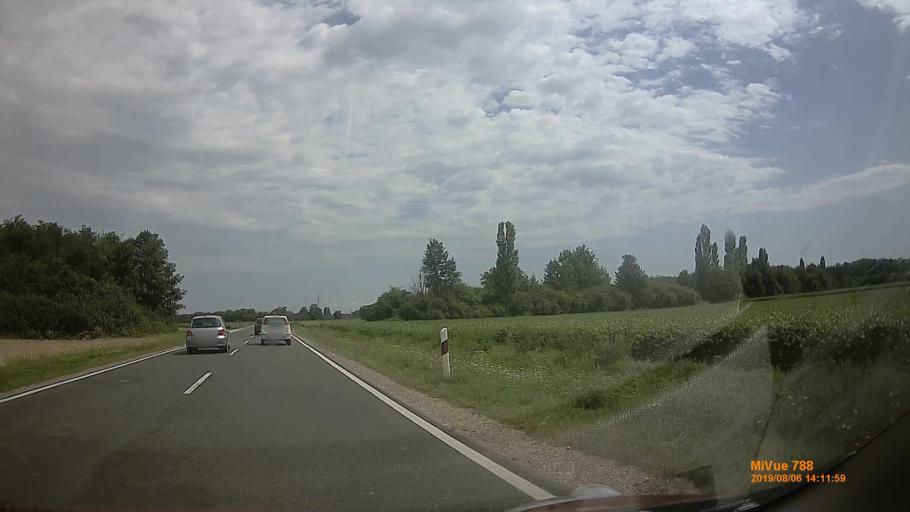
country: HU
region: Vas
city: Taplanszentkereszt
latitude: 47.2131
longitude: 16.6734
